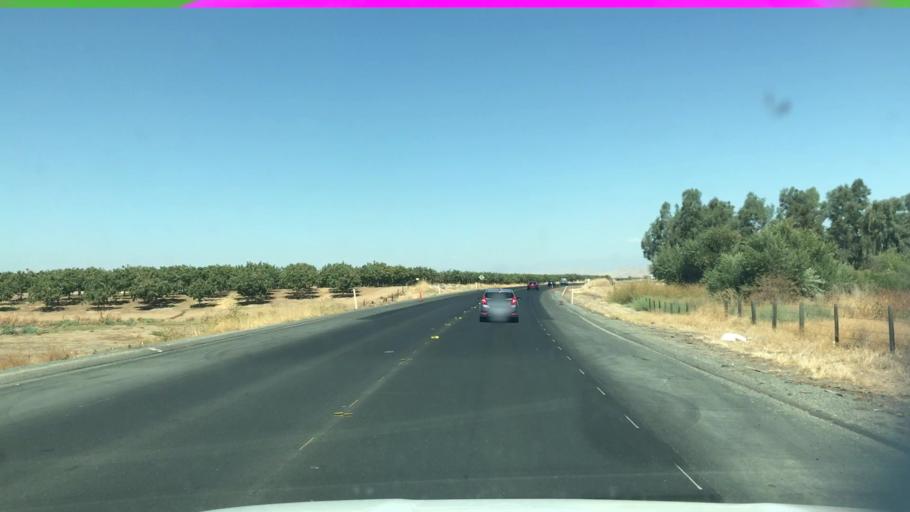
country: US
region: California
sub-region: Tulare County
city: Terra Bella
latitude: 35.9805
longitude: -119.0534
